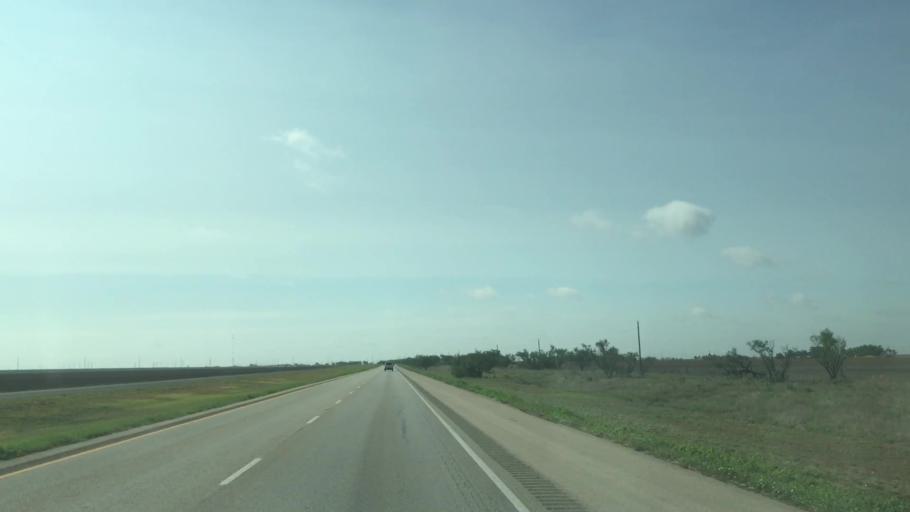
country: US
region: Texas
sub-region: Nolan County
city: Roscoe
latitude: 32.5834
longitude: -100.7270
